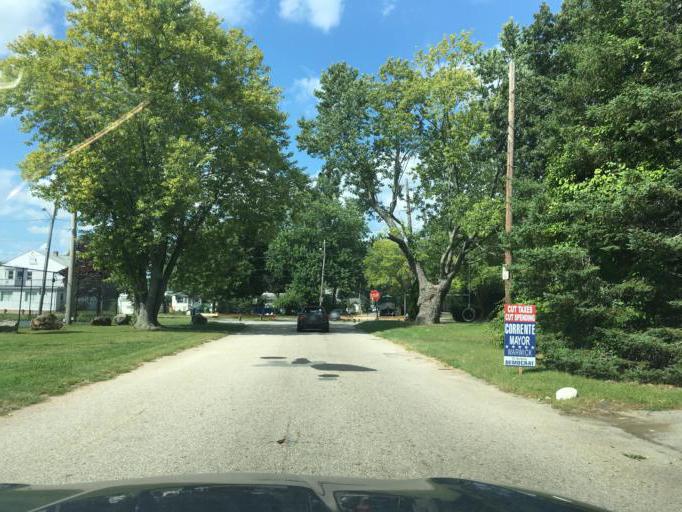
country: US
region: Rhode Island
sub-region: Kent County
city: Warwick
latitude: 41.6862
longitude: -71.3973
